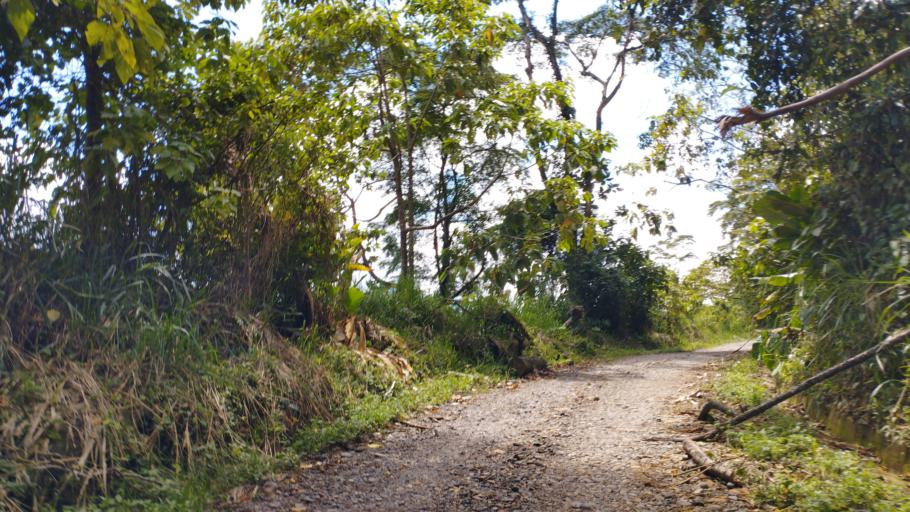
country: CO
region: Boyaca
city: San Luis de Gaceno
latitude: 4.7788
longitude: -73.1225
